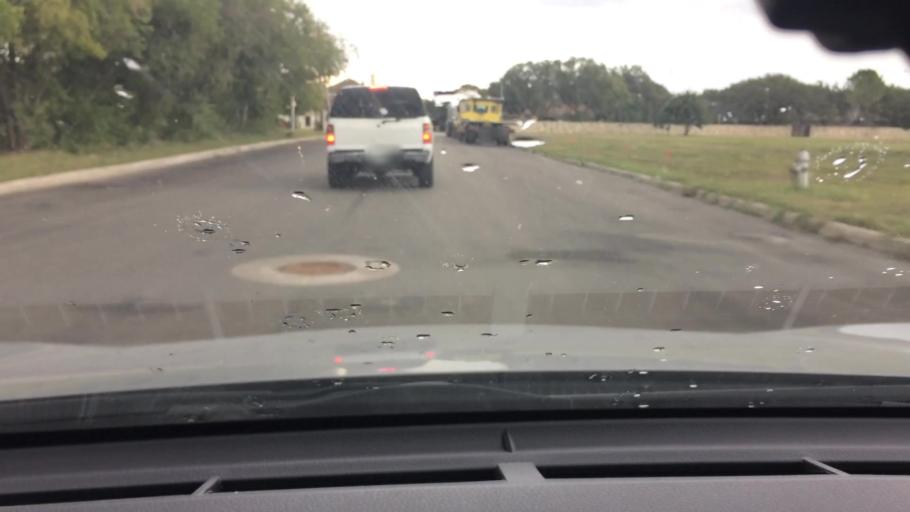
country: US
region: Texas
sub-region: Bexar County
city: Shavano Park
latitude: 29.5731
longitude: -98.5868
